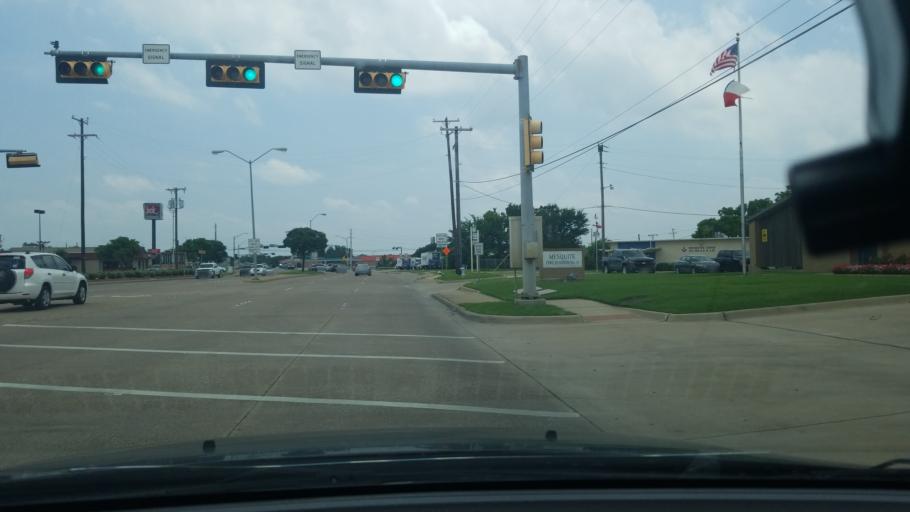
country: US
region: Texas
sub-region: Dallas County
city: Mesquite
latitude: 32.7947
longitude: -96.6120
